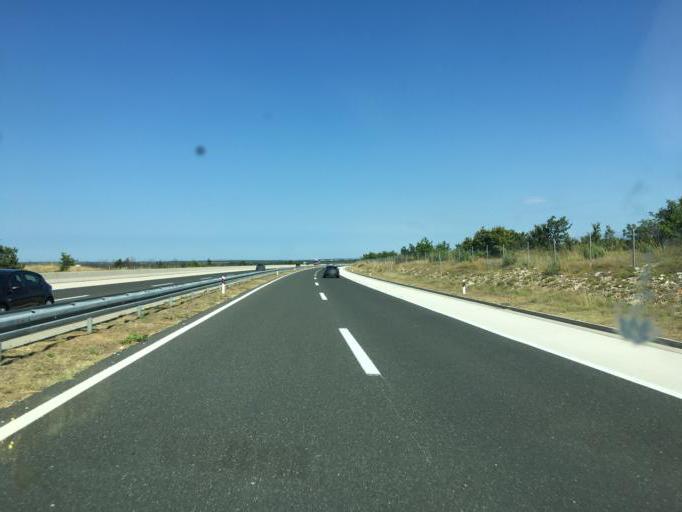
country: HR
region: Zadarska
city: Galovac
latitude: 44.1235
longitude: 15.4311
